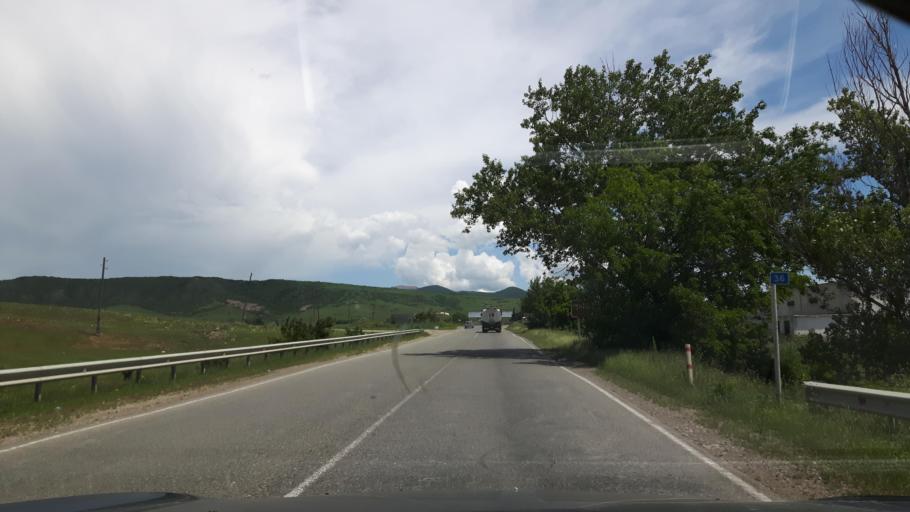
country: GE
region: Kakheti
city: Sagarejo
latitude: 41.7286
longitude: 45.1918
